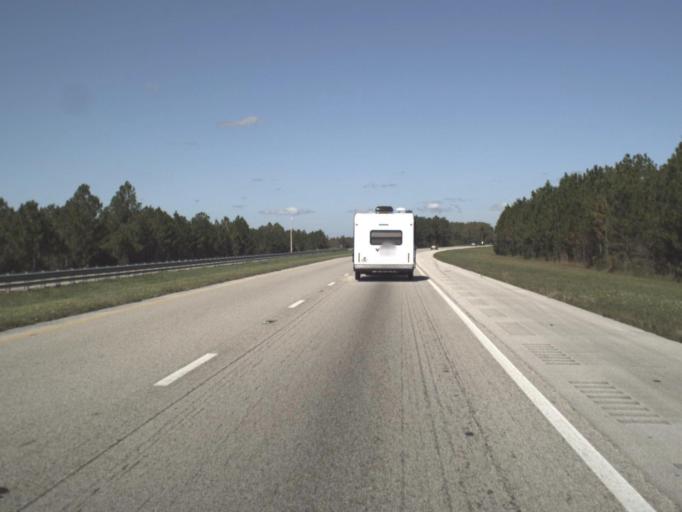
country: US
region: Florida
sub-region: Osceola County
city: Saint Cloud
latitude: 27.9584
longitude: -81.0967
